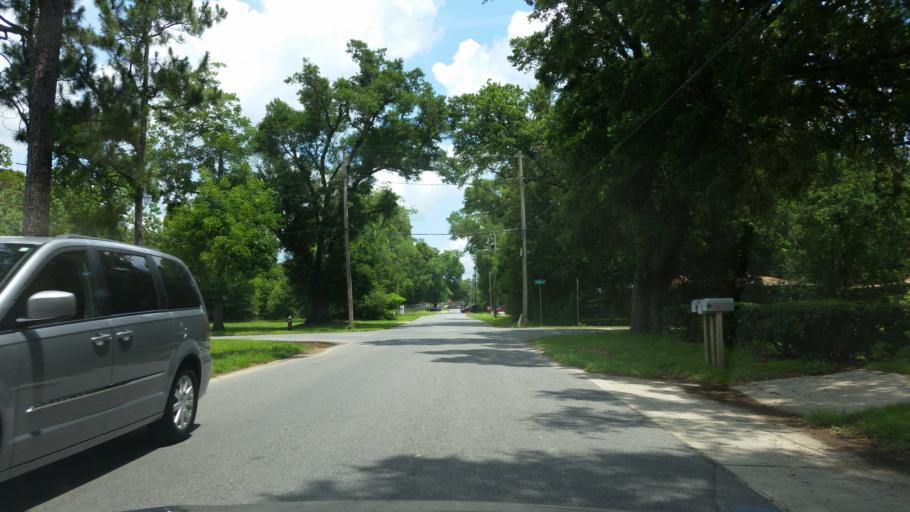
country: US
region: Florida
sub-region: Escambia County
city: Ensley
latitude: 30.5161
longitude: -87.2677
